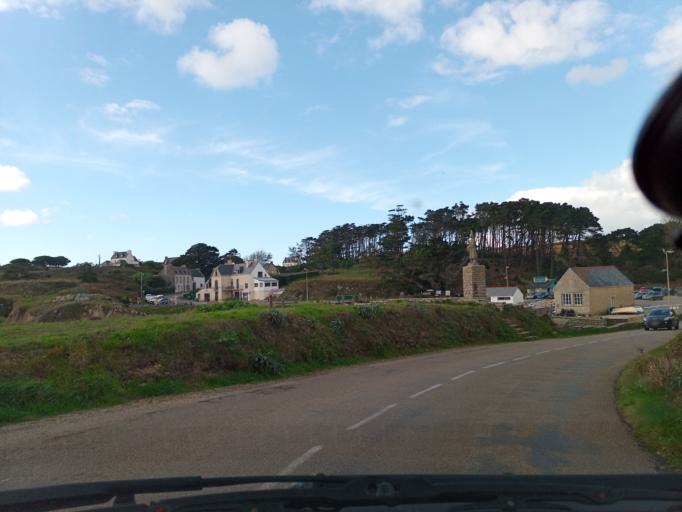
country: FR
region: Brittany
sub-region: Departement du Finistere
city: Plouhinec
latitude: 47.9851
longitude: -4.4622
